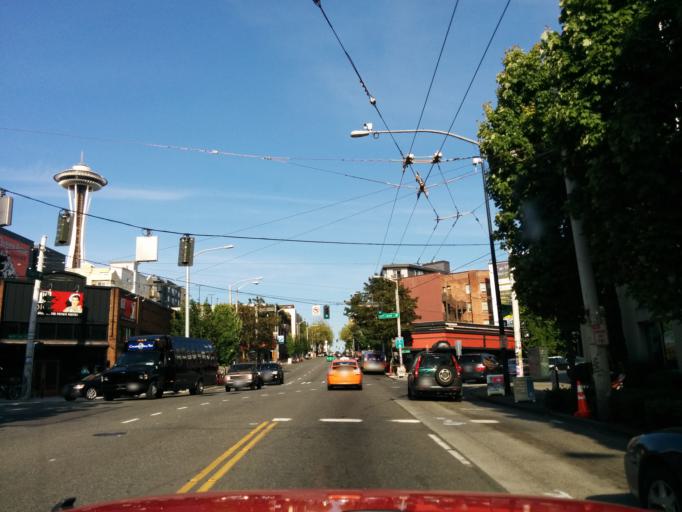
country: US
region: Washington
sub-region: King County
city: Seattle
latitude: 47.6186
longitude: -122.3558
